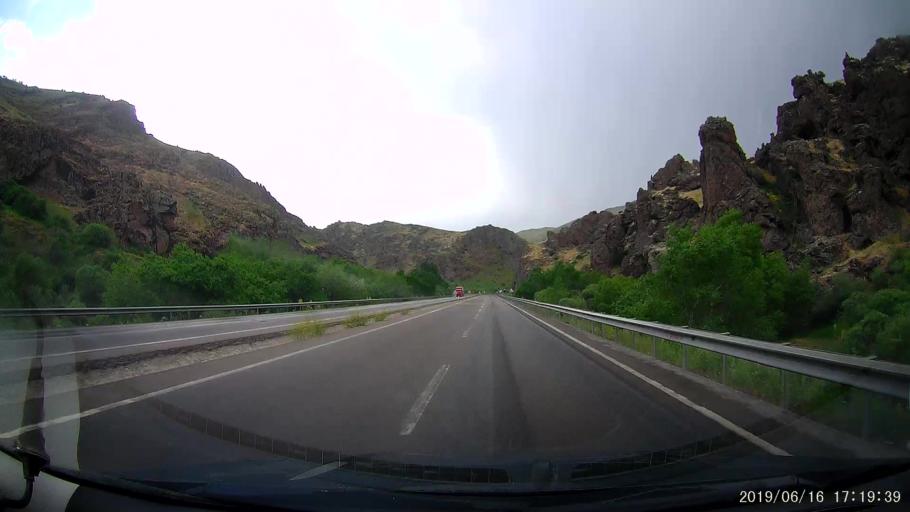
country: TR
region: Erzincan
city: Tercan
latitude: 39.8007
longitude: 40.5259
